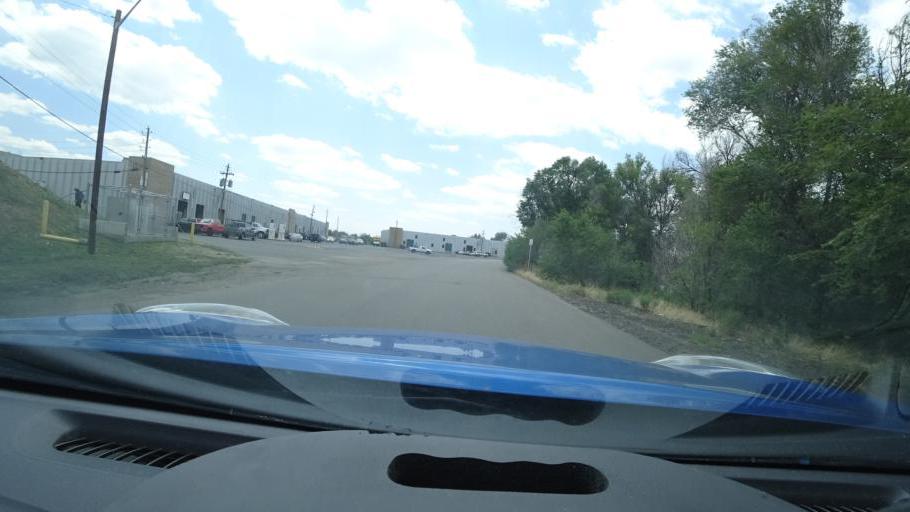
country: US
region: Colorado
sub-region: Arapahoe County
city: Englewood
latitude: 39.6693
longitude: -104.9983
